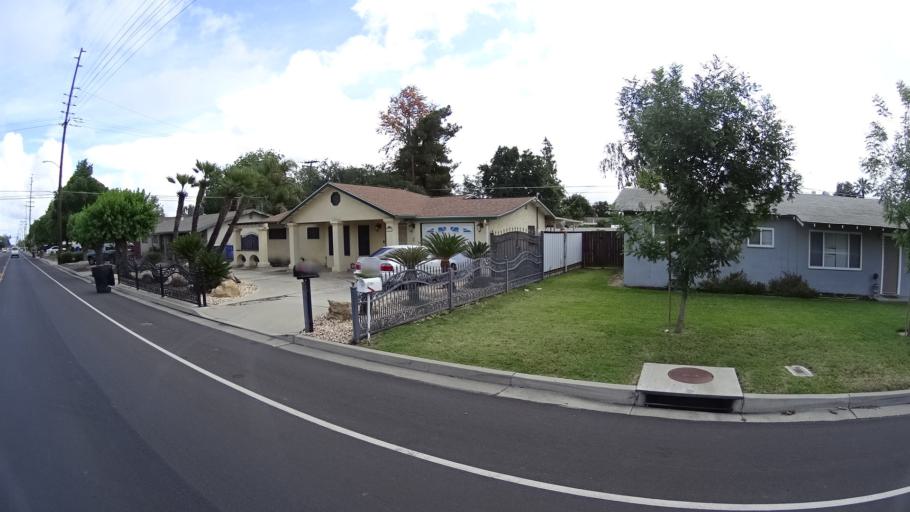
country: US
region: California
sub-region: Kings County
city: Hanford
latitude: 36.3495
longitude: -119.6551
